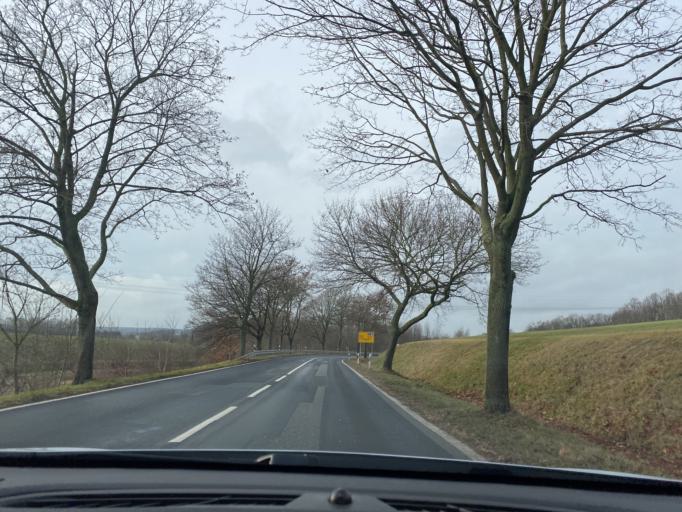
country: DE
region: Saxony
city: Markersdorf
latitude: 51.1468
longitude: 14.9181
